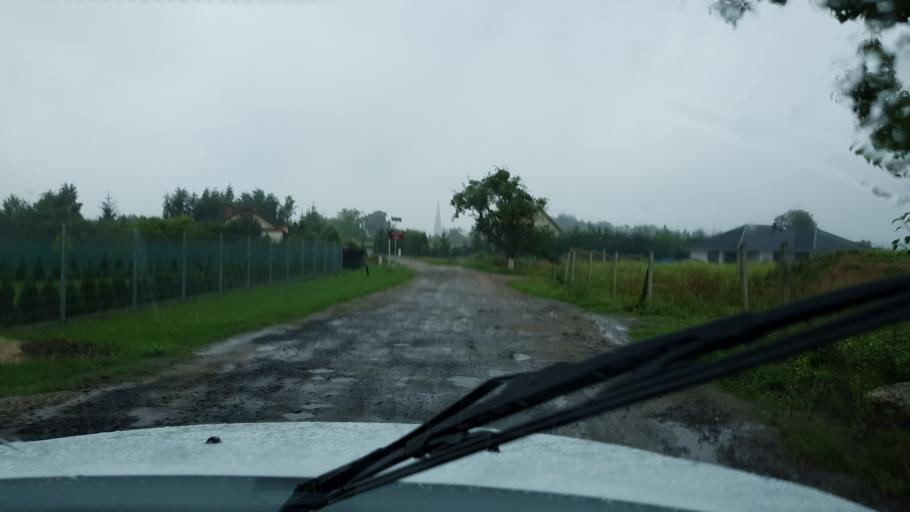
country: PL
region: West Pomeranian Voivodeship
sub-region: Powiat gryfinski
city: Chojna
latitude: 52.9520
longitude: 14.4259
